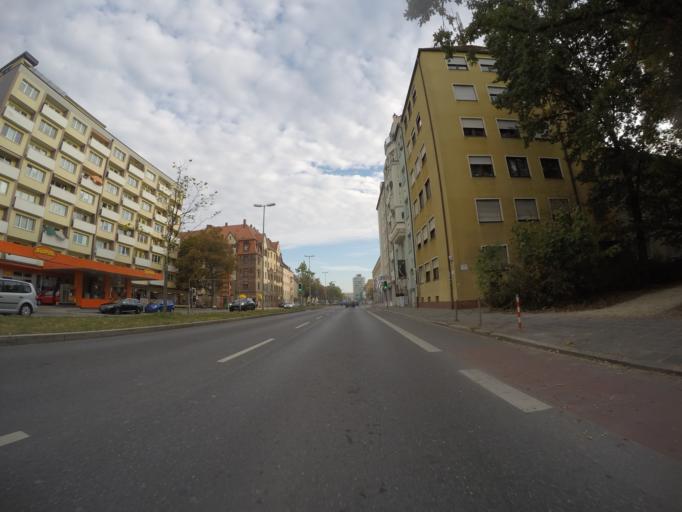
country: DE
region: Bavaria
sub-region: Regierungsbezirk Mittelfranken
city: Nuernberg
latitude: 49.4694
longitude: 11.1004
